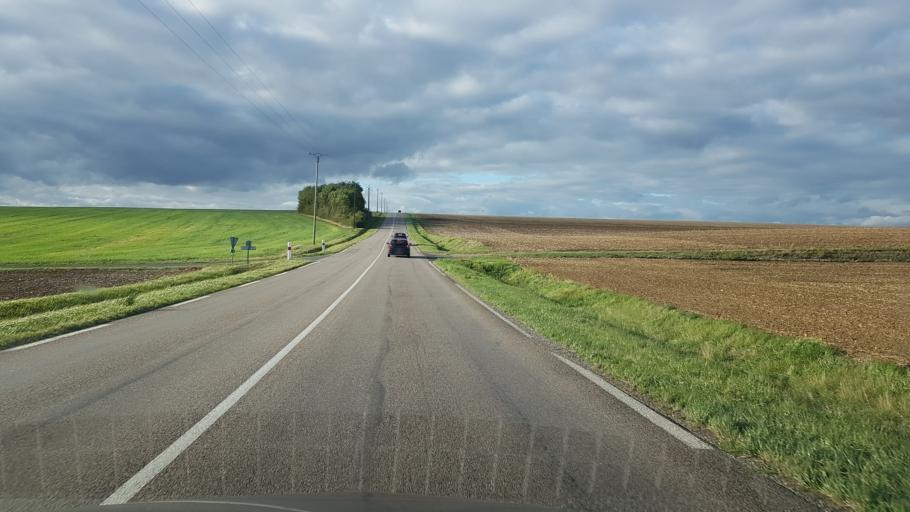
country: FR
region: Centre
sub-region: Departement du Loiret
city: Sermaises
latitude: 48.3383
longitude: 2.1885
